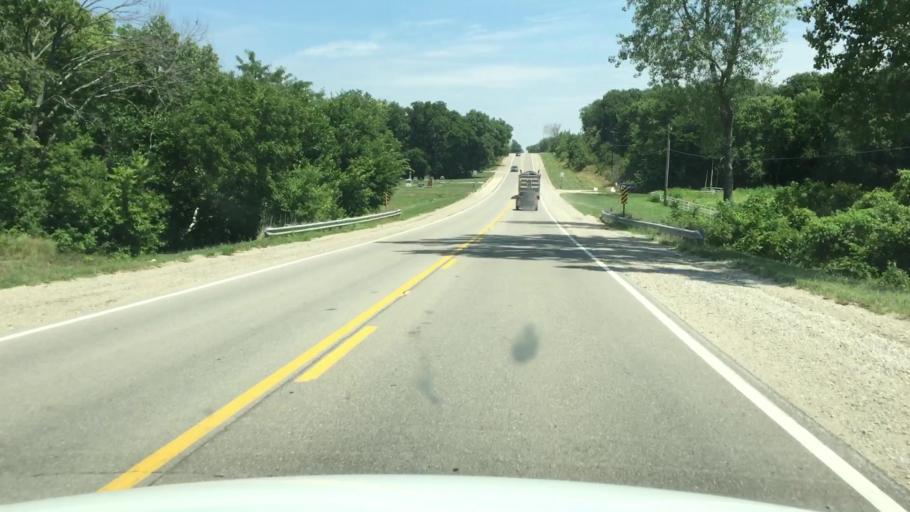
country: US
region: Kansas
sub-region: Shawnee County
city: Topeka
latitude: 38.9861
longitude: -95.5786
